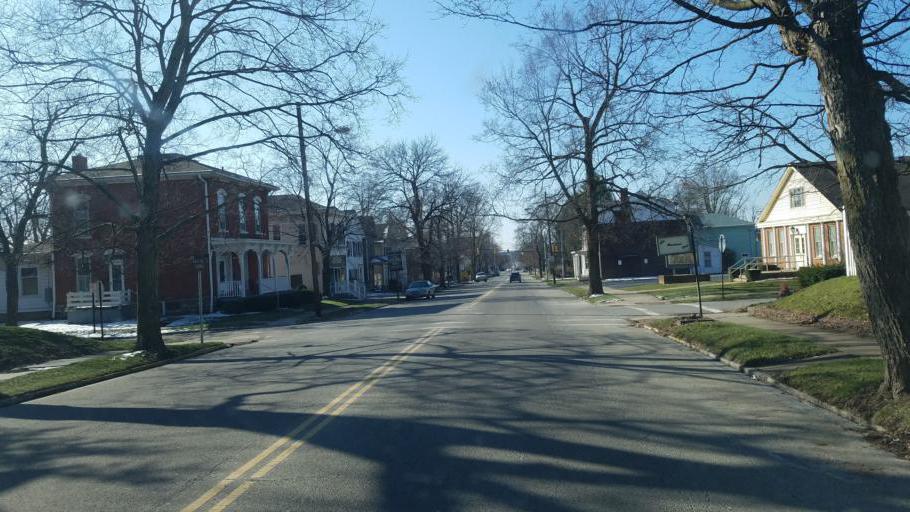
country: US
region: Ohio
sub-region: Knox County
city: Mount Vernon
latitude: 40.3995
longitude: -82.4850
